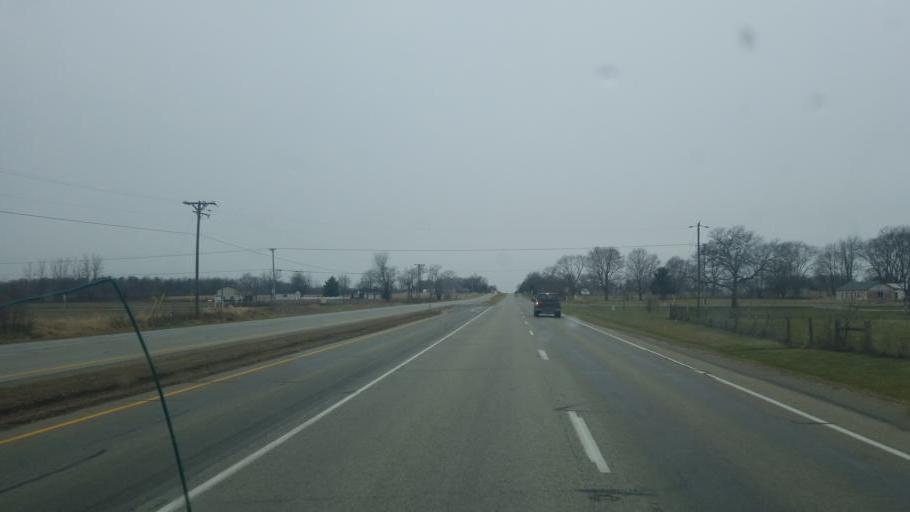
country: US
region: Indiana
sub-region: Hancock County
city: Greenfield
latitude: 39.7888
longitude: -85.6875
